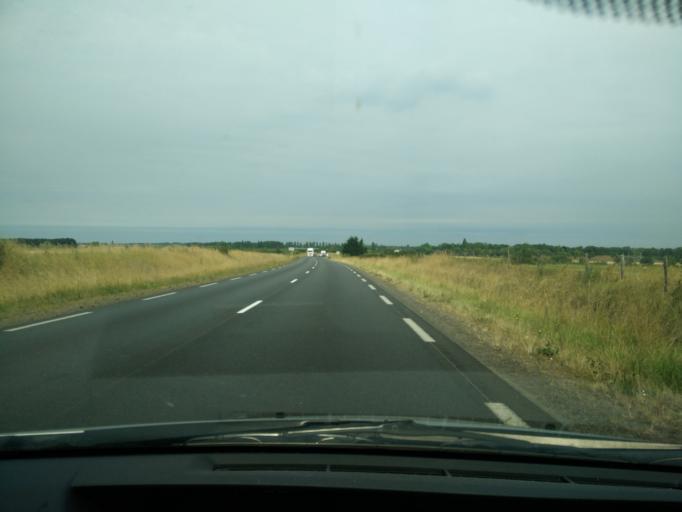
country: FR
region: Pays de la Loire
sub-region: Departement de Maine-et-Loire
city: Doue-la-Fontaine
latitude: 47.1839
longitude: -0.2919
